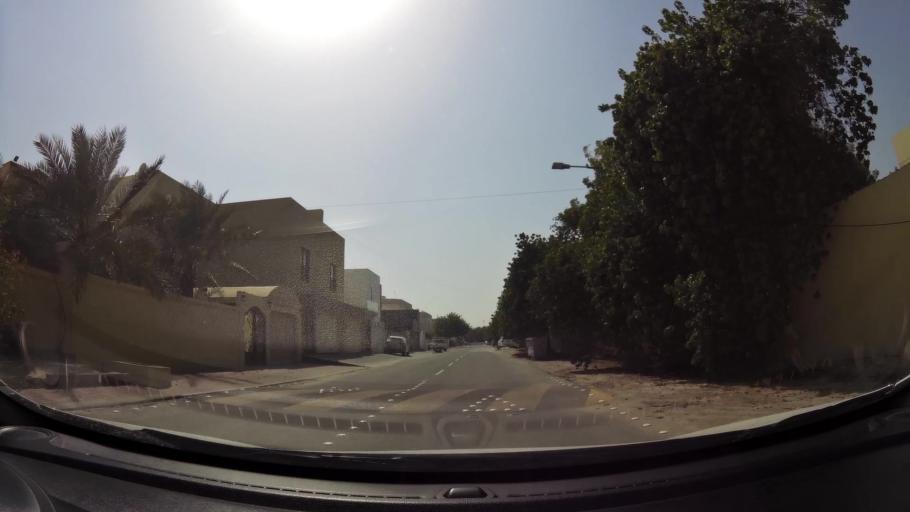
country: BH
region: Manama
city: Jidd Hafs
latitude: 26.1995
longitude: 50.4626
